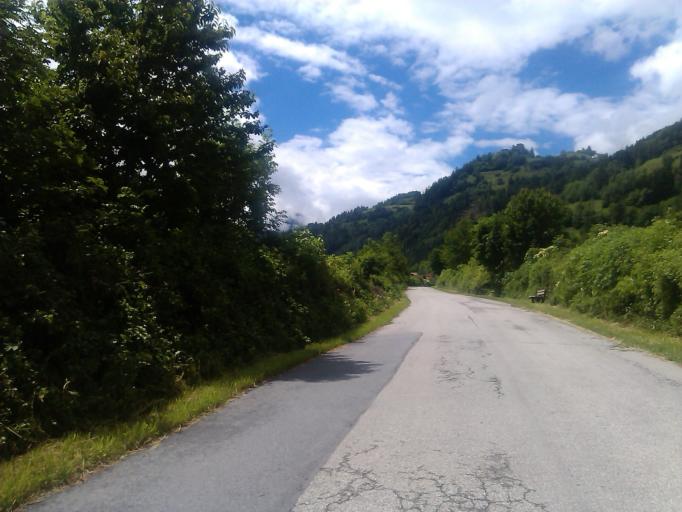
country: AT
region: Tyrol
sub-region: Politischer Bezirk Landeck
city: Prutz
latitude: 47.0884
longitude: 10.6629
